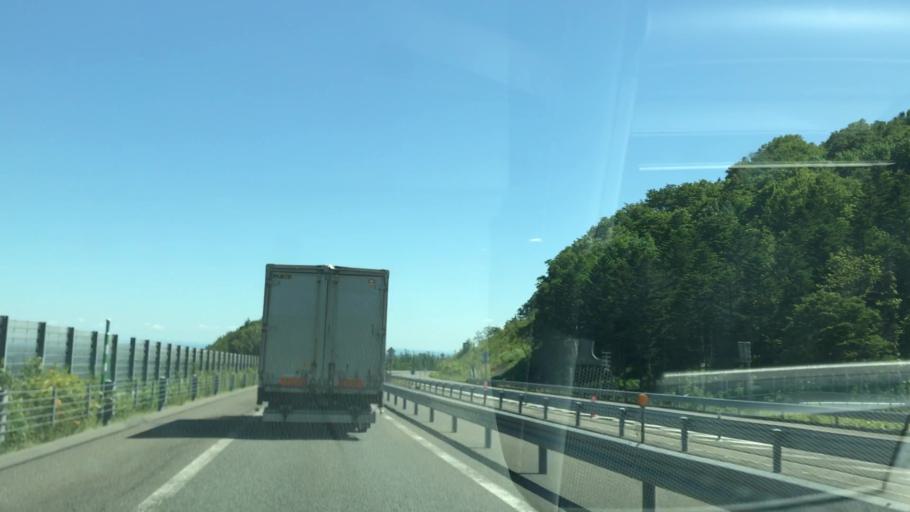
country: JP
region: Hokkaido
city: Otofuke
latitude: 43.0704
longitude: 142.7560
